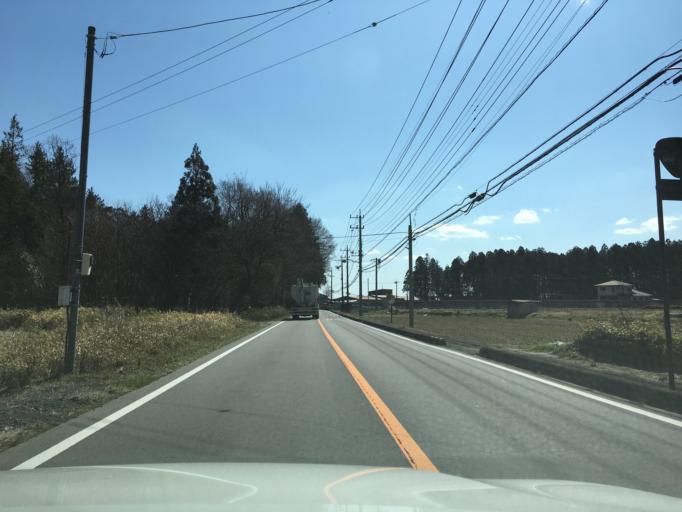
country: JP
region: Tochigi
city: Otawara
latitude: 36.8955
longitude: 140.1182
